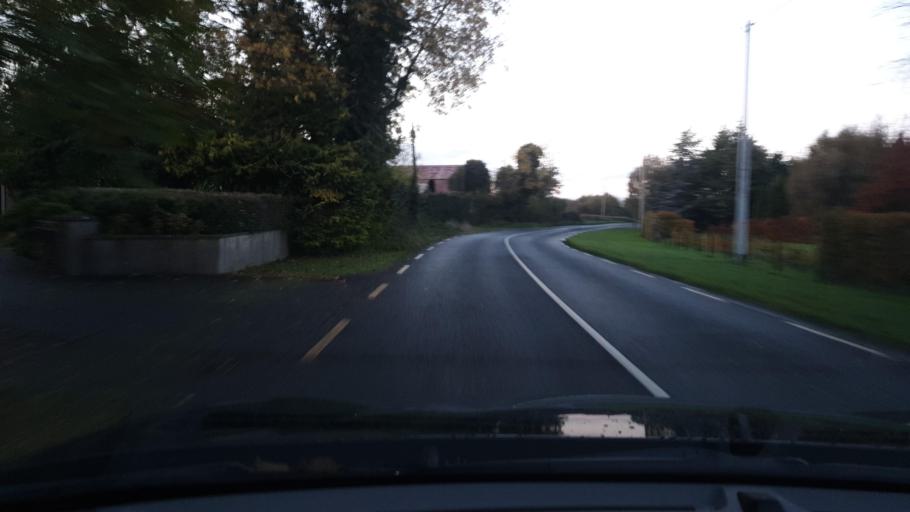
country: IE
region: Leinster
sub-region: An Mhi
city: Ratoath
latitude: 53.4972
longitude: -6.4402
